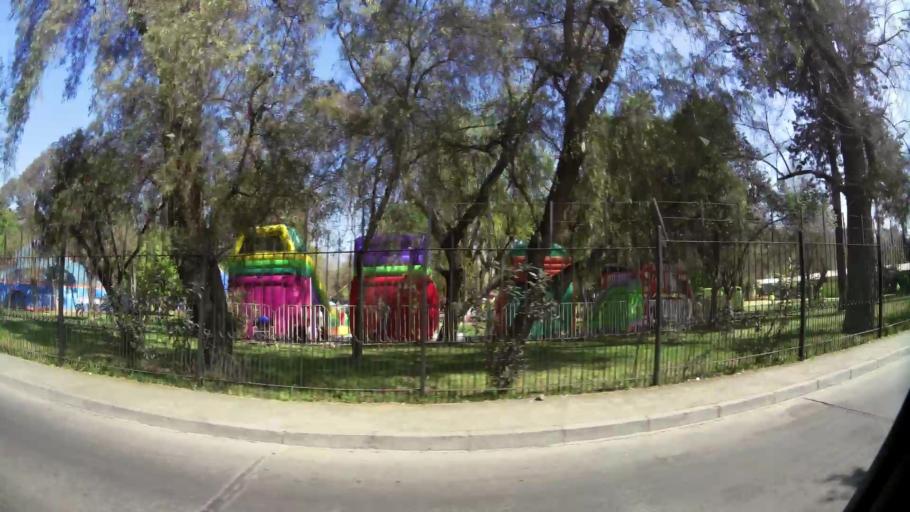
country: CL
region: Santiago Metropolitan
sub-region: Provincia de Santiago
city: Santiago
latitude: -33.4689
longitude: -70.6573
